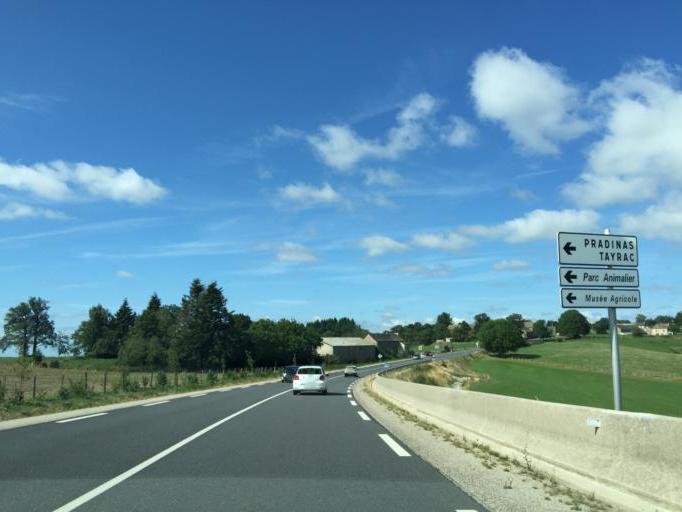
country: FR
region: Midi-Pyrenees
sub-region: Departement de l'Aveyron
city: Rieupeyroux
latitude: 44.3043
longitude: 2.2673
